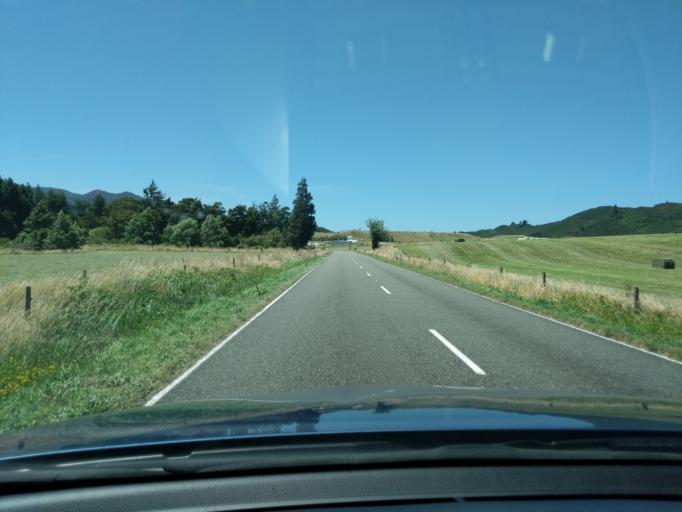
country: NZ
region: Tasman
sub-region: Tasman District
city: Takaka
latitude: -40.7495
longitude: 172.5635
